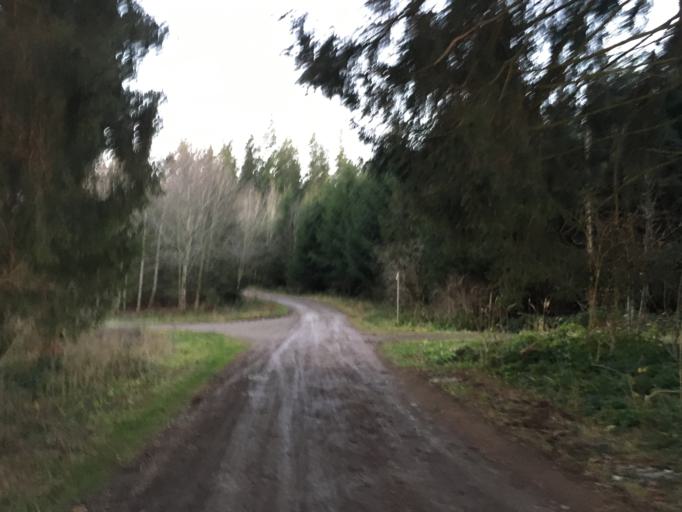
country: DE
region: Bavaria
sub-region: Swabia
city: Bohen
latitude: 47.8719
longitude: 10.2808
